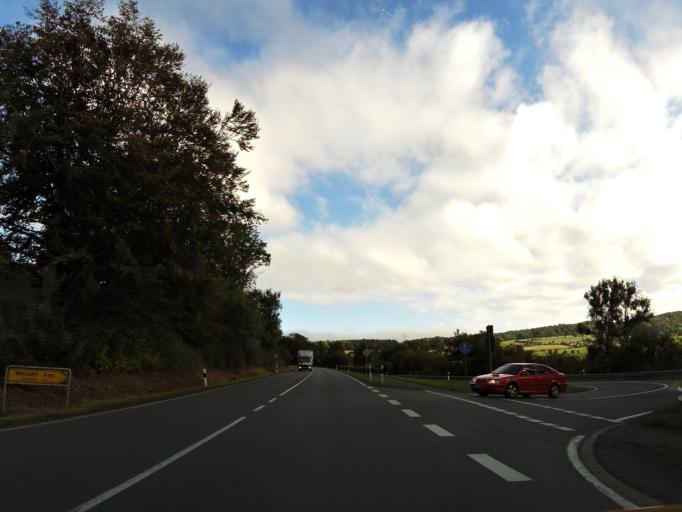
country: DE
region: Lower Saxony
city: Einbeck
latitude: 51.8410
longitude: 9.8419
